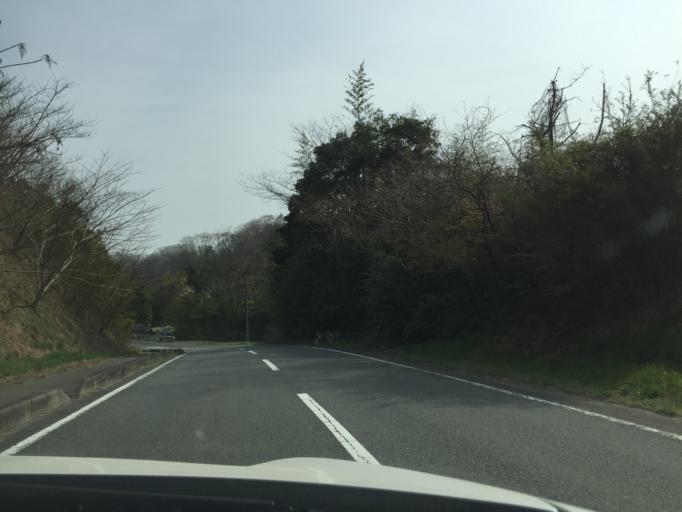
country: JP
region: Fukushima
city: Iwaki
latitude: 36.9977
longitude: 140.7896
